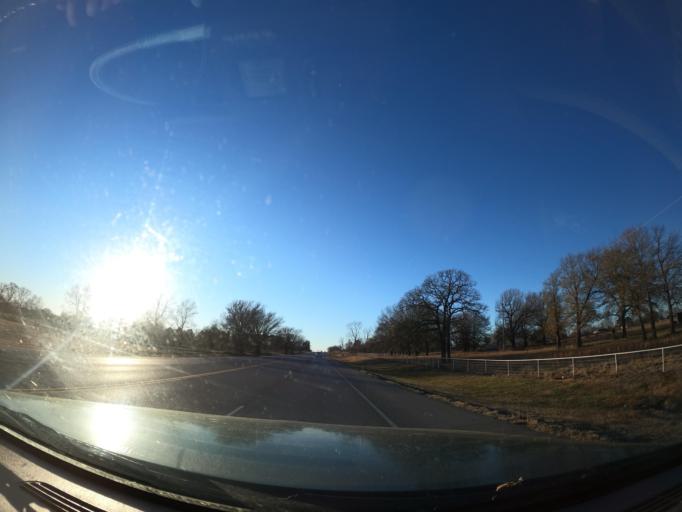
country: US
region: Oklahoma
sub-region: Pittsburg County
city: Krebs
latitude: 34.8942
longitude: -95.6434
